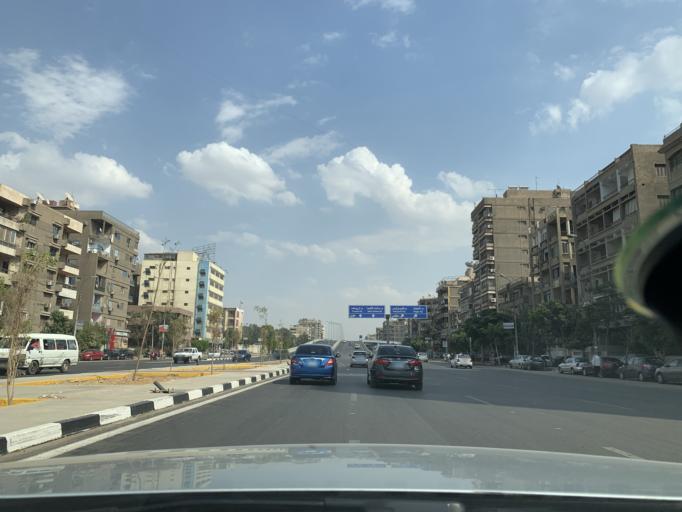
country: EG
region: Muhafazat al Qalyubiyah
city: Al Khankah
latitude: 30.1142
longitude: 31.3437
